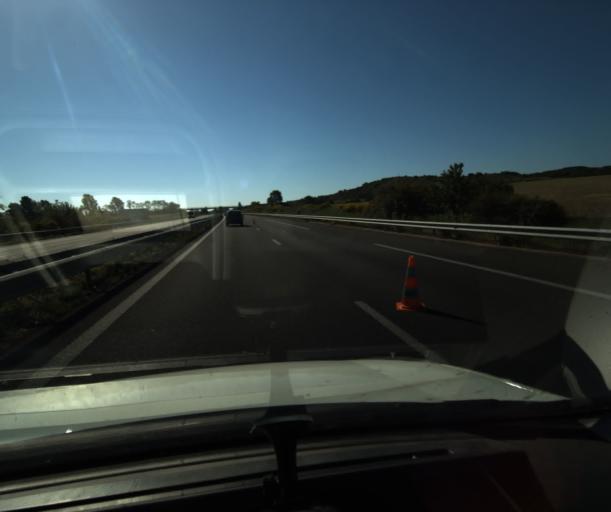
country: FR
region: Midi-Pyrenees
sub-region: Departement de la Haute-Garonne
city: Avignonet-Lauragais
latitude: 43.3250
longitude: 1.8564
